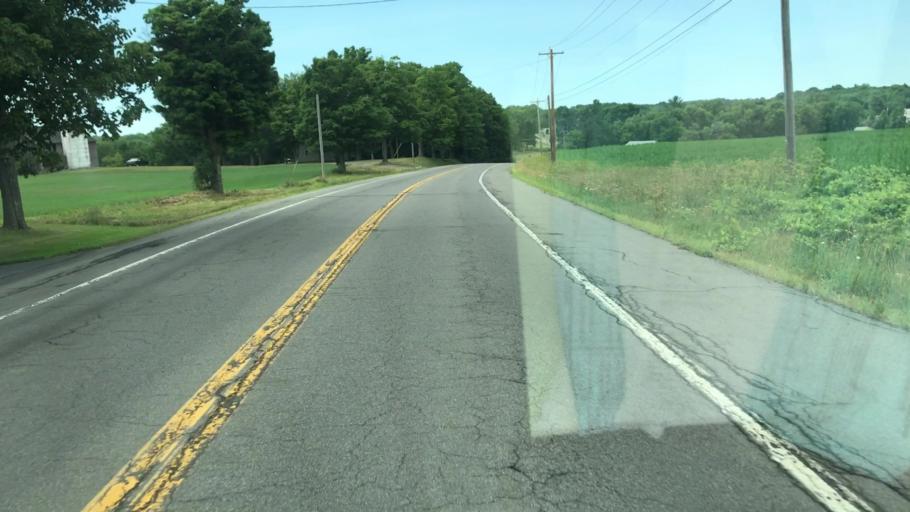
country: US
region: New York
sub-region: Onondaga County
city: Skaneateles
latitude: 42.9418
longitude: -76.3851
